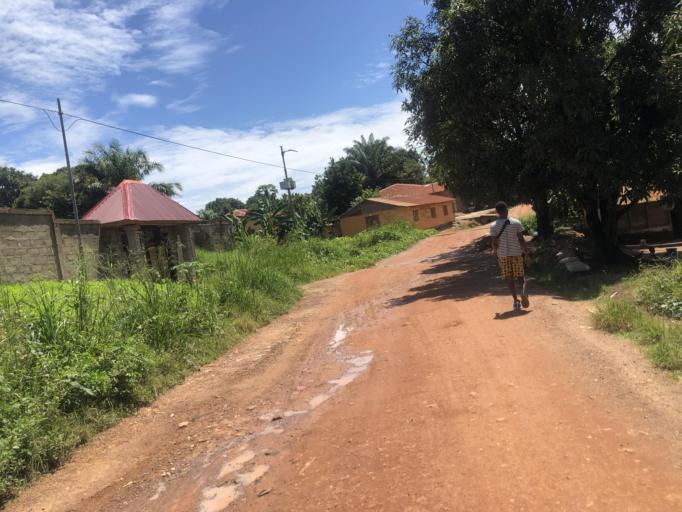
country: SL
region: Eastern Province
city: Koidu
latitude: 8.6404
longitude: -10.9649
